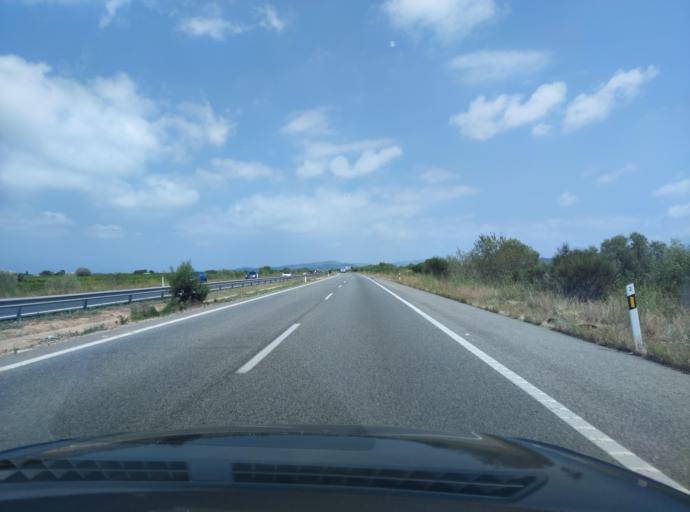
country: ES
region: Catalonia
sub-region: Provincia de Tarragona
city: Alcanar
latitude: 40.5273
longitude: 0.4180
